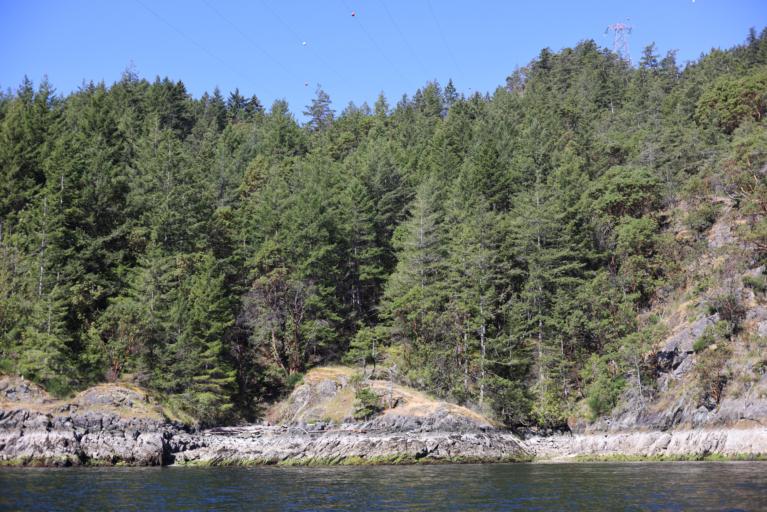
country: CA
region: British Columbia
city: North Cowichan
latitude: 48.8275
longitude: -123.5842
